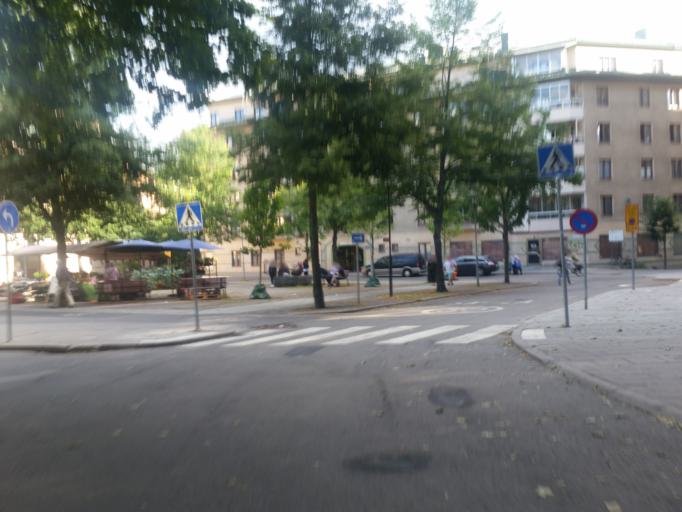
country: SE
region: Stockholm
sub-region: Stockholms Kommun
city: OEstermalm
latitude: 59.3079
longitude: 18.0901
